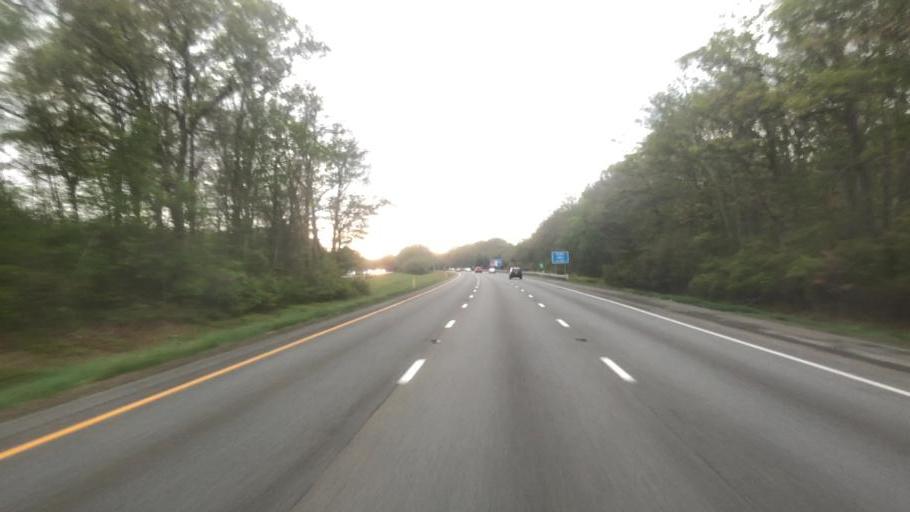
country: US
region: Massachusetts
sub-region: Bristol County
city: Ocean Grove
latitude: 41.7609
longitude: -71.2302
